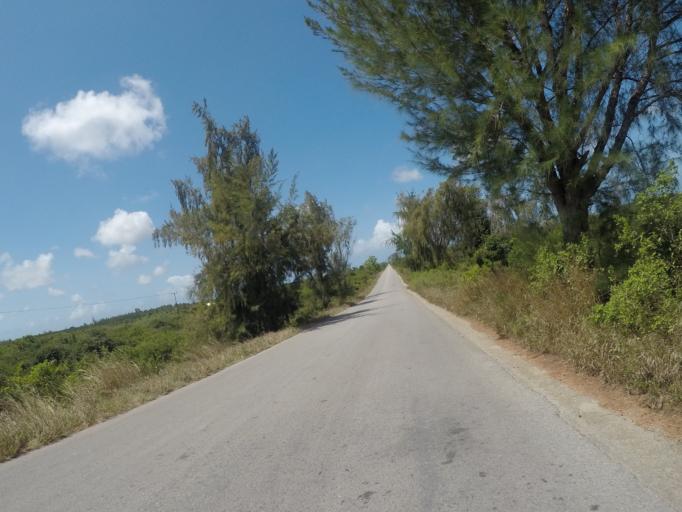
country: TZ
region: Zanzibar Central/South
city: Nganane
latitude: -6.2810
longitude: 39.4743
